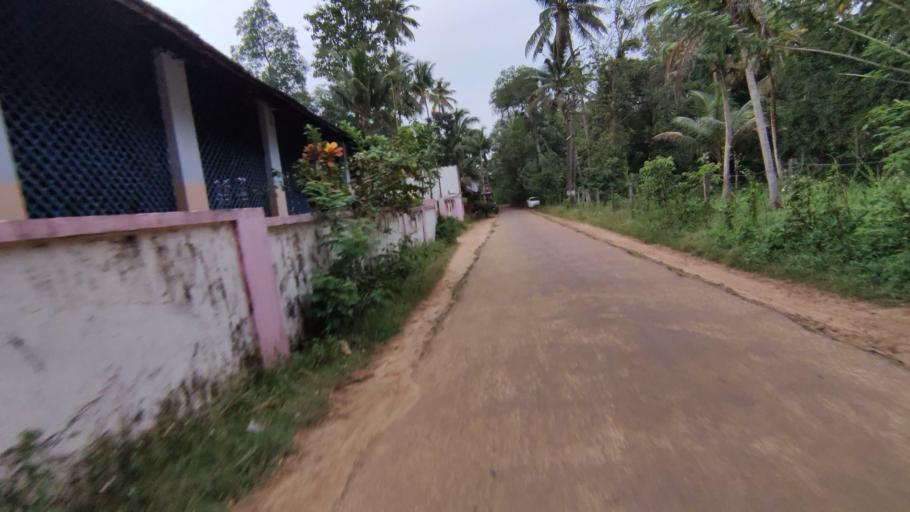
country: IN
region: Kerala
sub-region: Alappuzha
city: Shertallai
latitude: 9.6611
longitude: 76.3638
